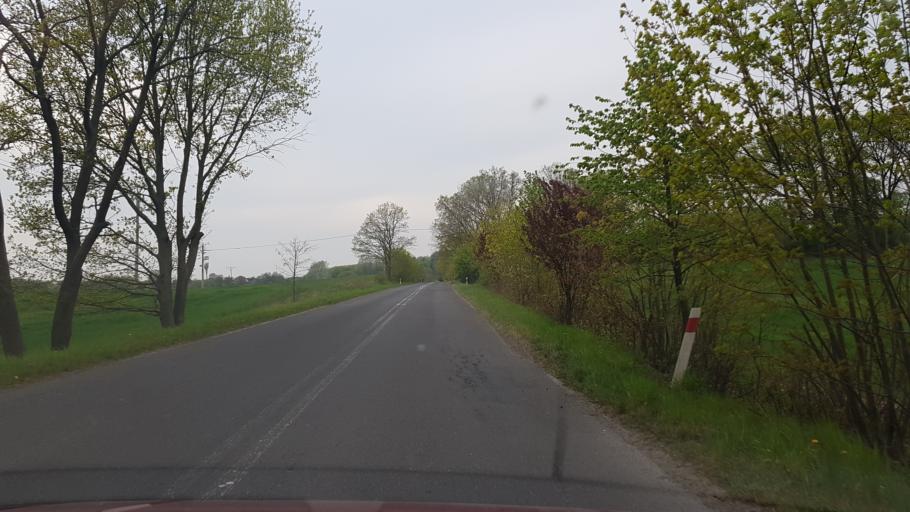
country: PL
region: West Pomeranian Voivodeship
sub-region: Powiat gryfinski
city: Stare Czarnowo
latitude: 53.2871
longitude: 14.7397
